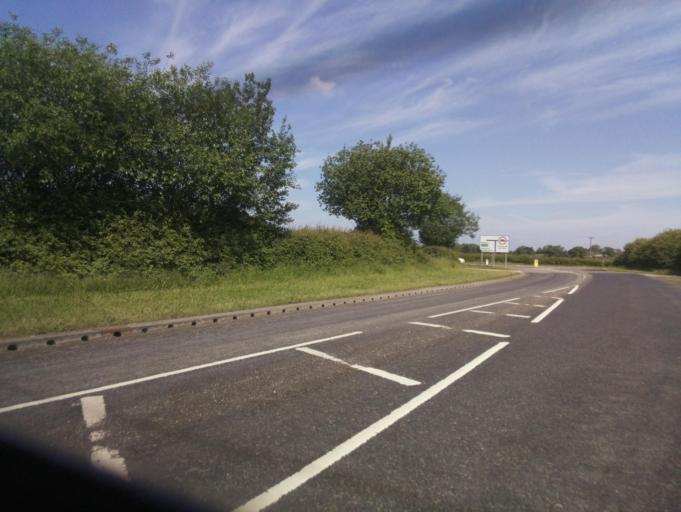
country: GB
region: England
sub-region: Lincolnshire
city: Skellingthorpe
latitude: 53.1702
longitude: -0.6423
